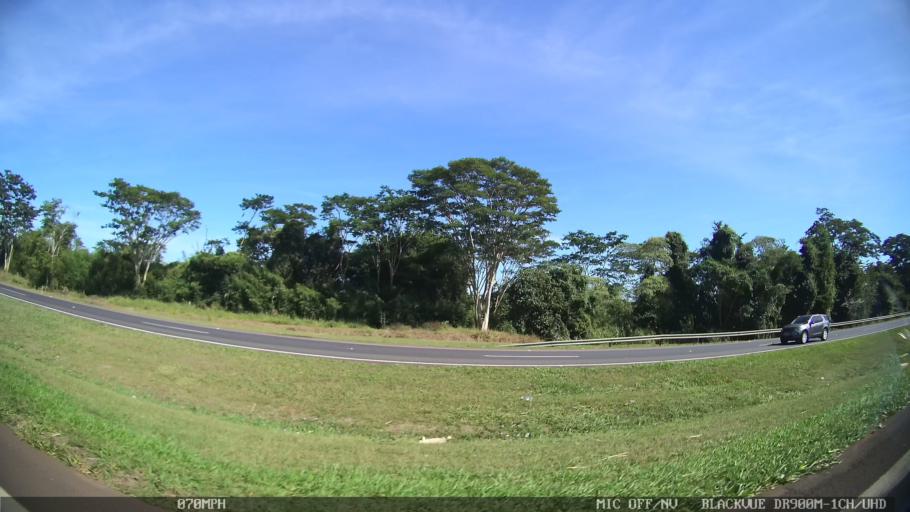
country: BR
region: Sao Paulo
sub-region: Porto Ferreira
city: Porto Ferreira
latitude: -21.8160
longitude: -47.4972
